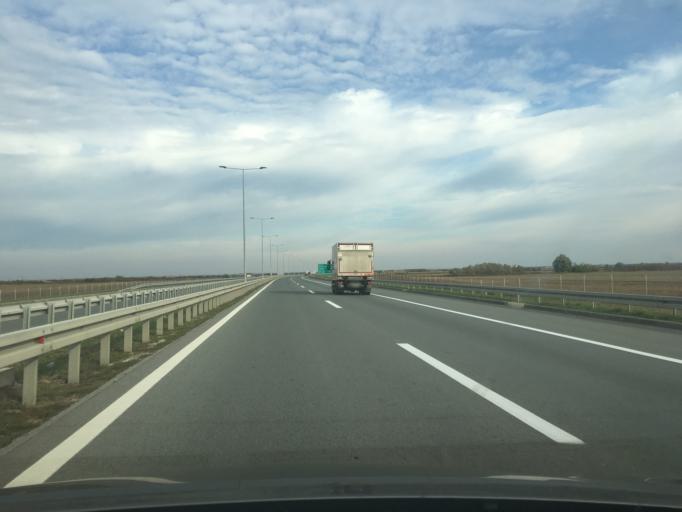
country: RS
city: Dobanovci
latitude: 44.8472
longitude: 20.2495
